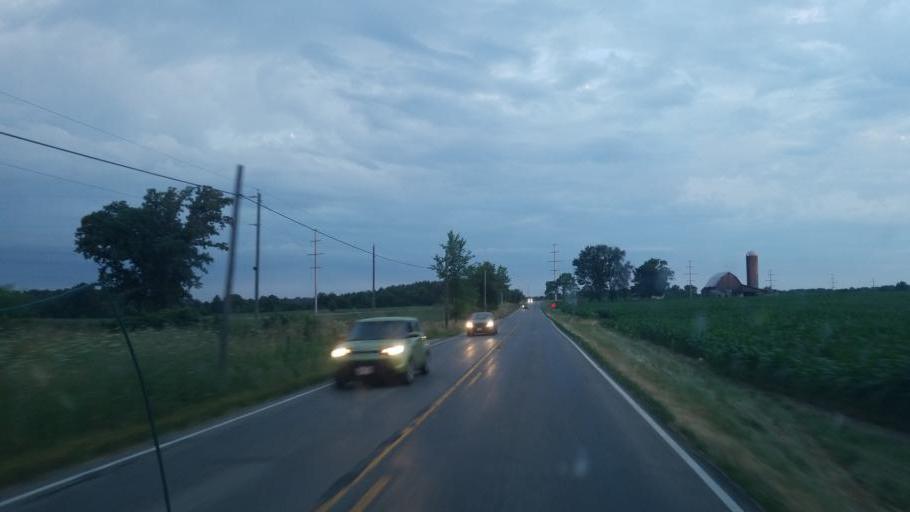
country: US
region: Ohio
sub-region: Defiance County
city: Hicksville
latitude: 41.3367
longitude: -84.8208
